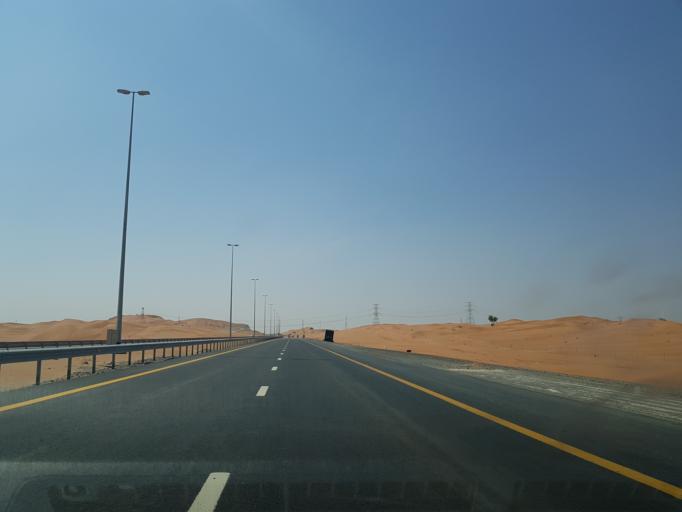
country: AE
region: Ash Shariqah
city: Adh Dhayd
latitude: 25.2451
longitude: 55.8557
